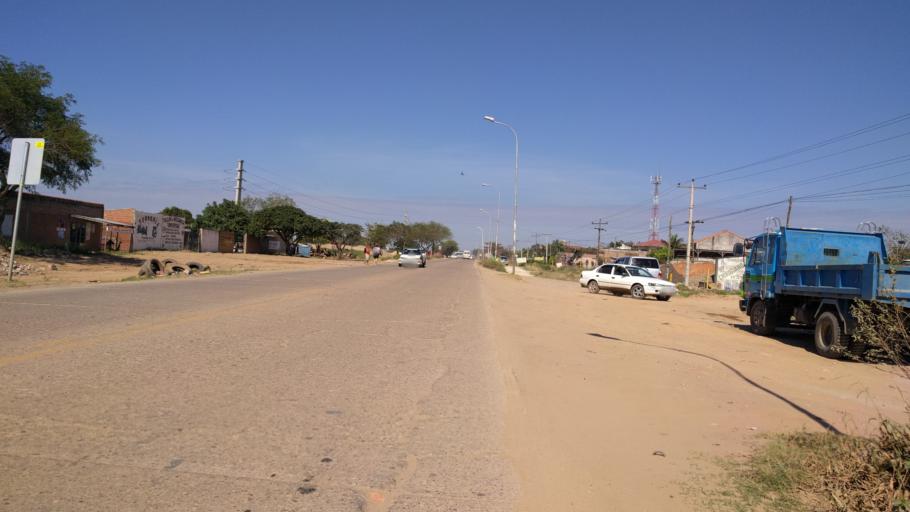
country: BO
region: Santa Cruz
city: Santa Cruz de la Sierra
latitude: -17.8544
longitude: -63.1847
